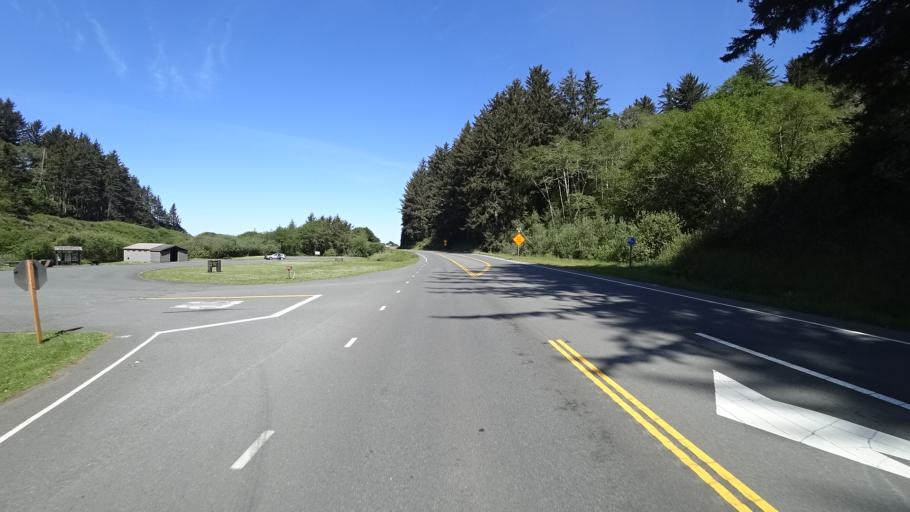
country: US
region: California
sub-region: Del Norte County
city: Bertsch-Oceanview
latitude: 41.5940
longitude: -124.0984
